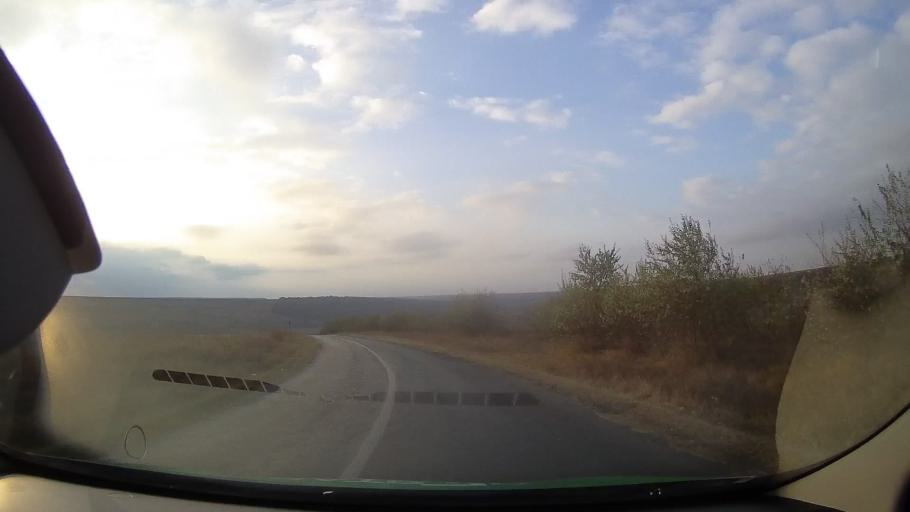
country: RO
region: Constanta
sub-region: Comuna Adamclisi
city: Adamclisi
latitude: 44.0206
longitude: 27.8847
